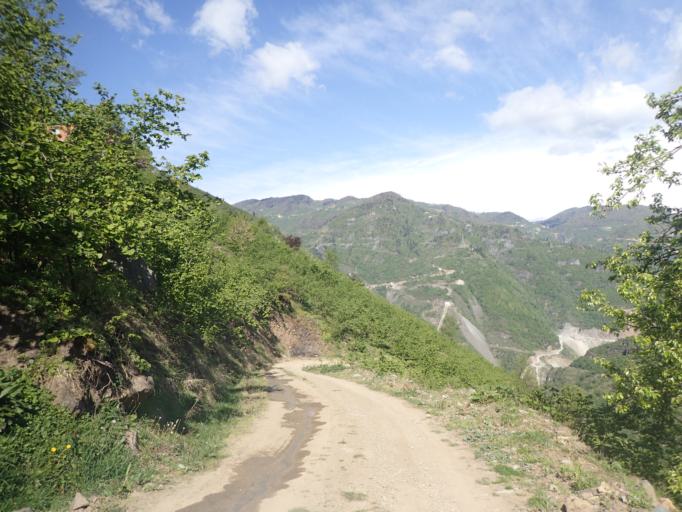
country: TR
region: Ordu
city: Topcam
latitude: 40.7083
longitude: 37.8764
